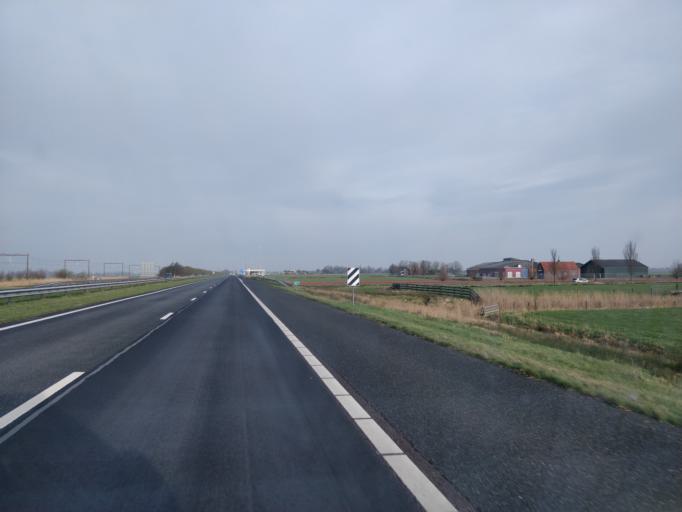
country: NL
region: Friesland
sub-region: Gemeente Boarnsterhim
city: Reduzum
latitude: 53.1226
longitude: 5.8077
